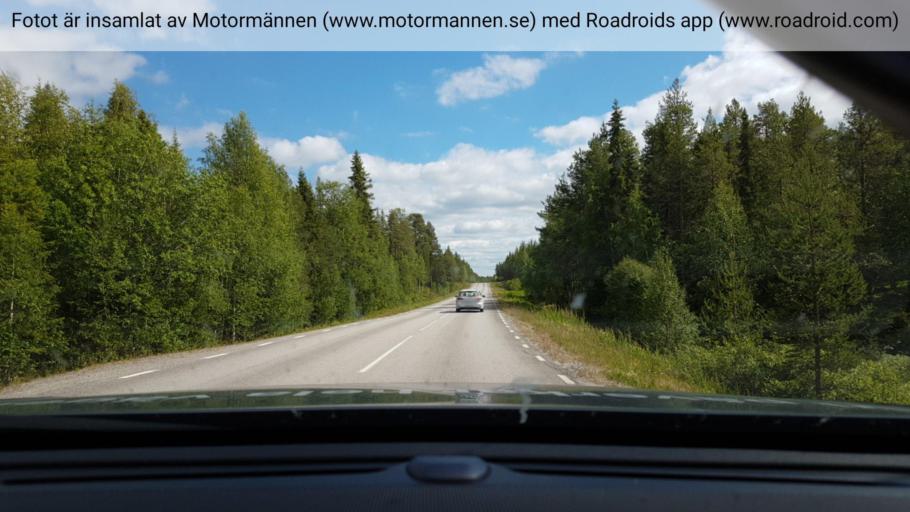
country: SE
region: Vaesterbotten
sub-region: Sorsele Kommun
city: Sorsele
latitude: 65.6003
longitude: 17.4937
